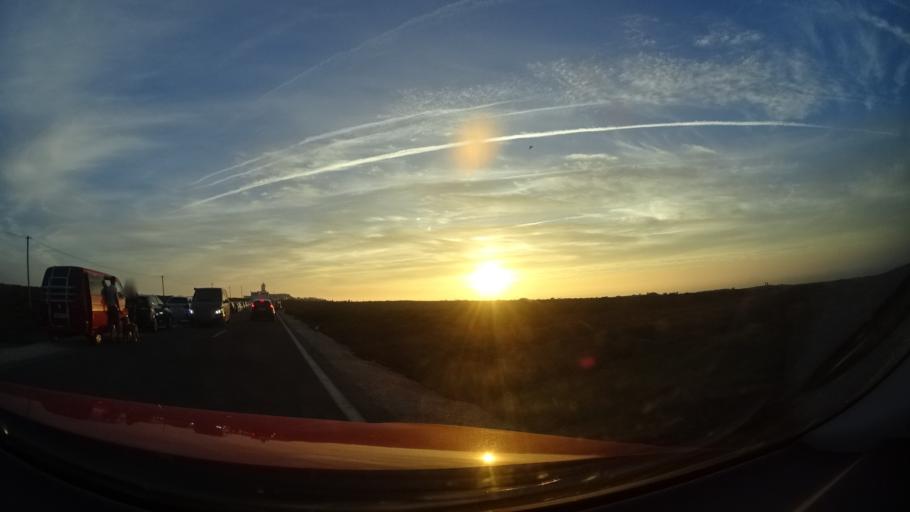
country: PT
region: Faro
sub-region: Vila do Bispo
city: Sagres
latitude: 37.0250
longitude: -8.9916
